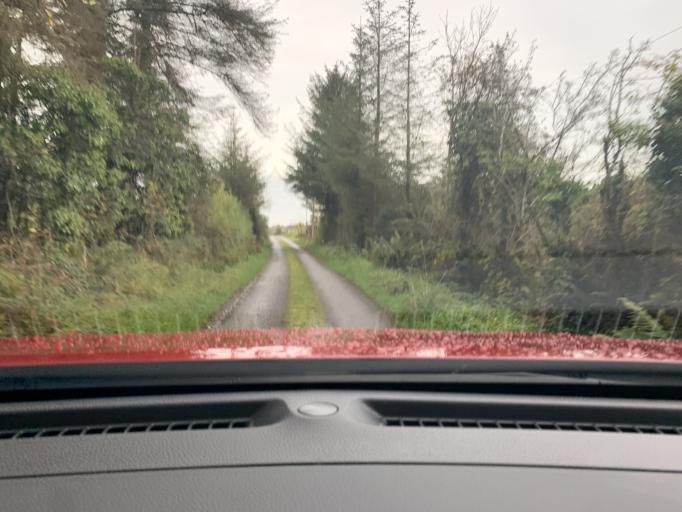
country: IE
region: Connaught
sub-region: Roscommon
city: Ballaghaderreen
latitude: 53.9178
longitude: -8.5670
